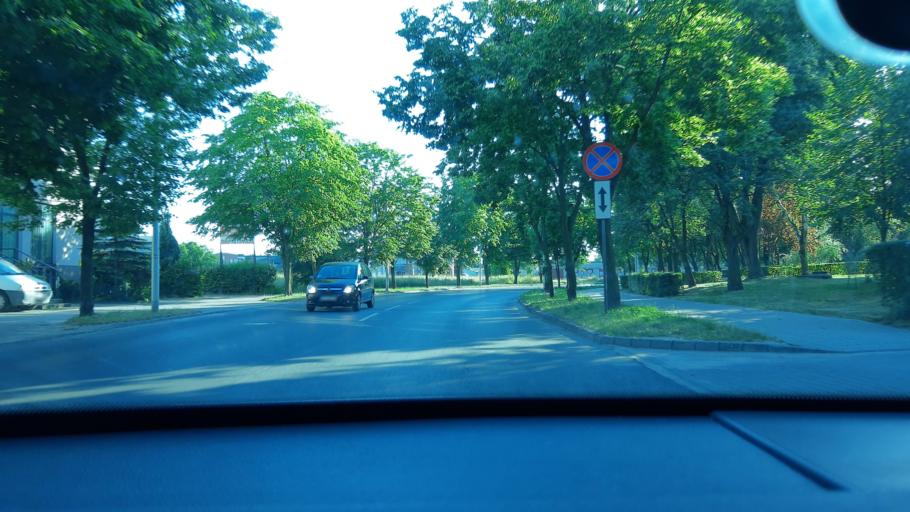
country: PL
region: Lodz Voivodeship
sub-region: Powiat sieradzki
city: Sieradz
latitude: 51.5864
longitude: 18.7268
